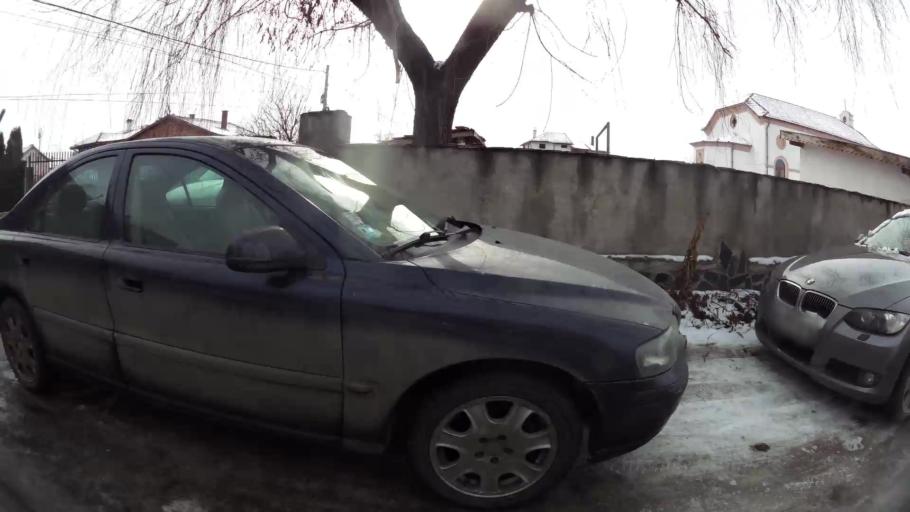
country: BG
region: Sofia-Capital
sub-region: Stolichna Obshtina
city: Sofia
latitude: 42.7139
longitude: 23.4145
